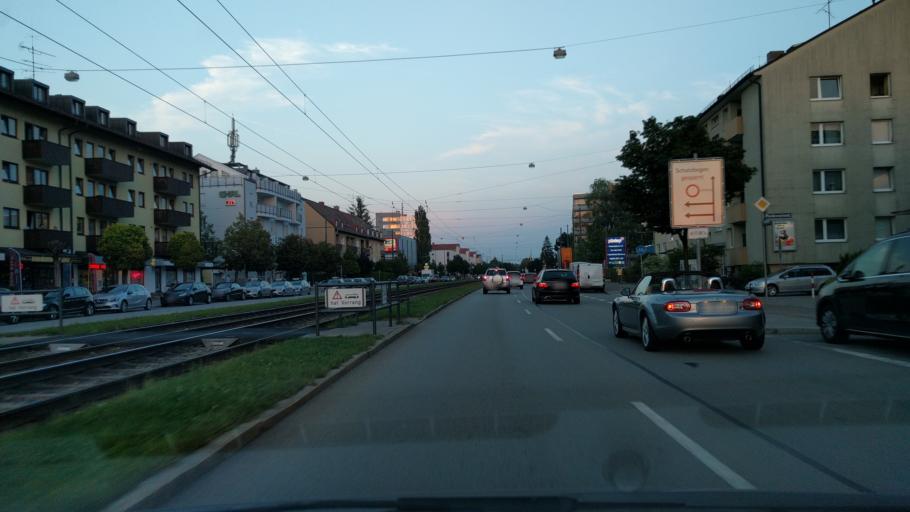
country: DE
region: Bavaria
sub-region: Upper Bavaria
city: Bogenhausen
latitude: 48.1264
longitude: 11.6418
